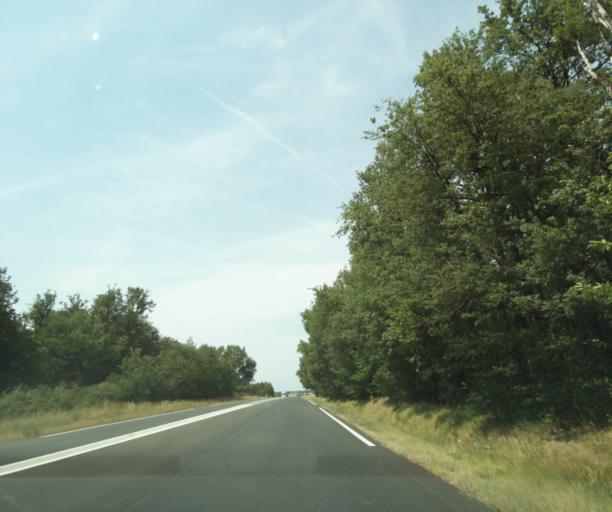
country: FR
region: Centre
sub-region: Departement d'Indre-et-Loire
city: Sainte-Maure-de-Touraine
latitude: 47.0689
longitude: 0.6144
